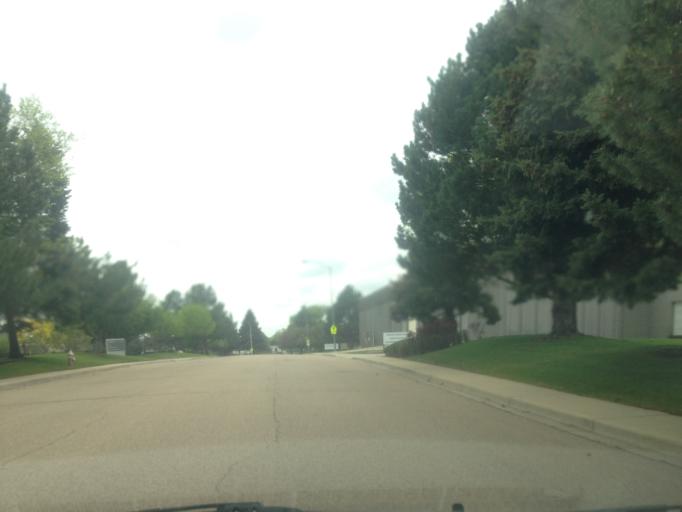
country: US
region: Colorado
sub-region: Boulder County
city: Longmont
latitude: 40.1420
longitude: -105.1248
